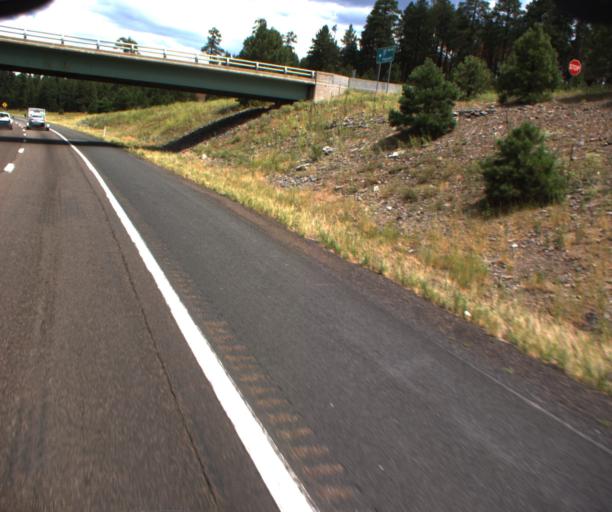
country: US
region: Arizona
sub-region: Coconino County
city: Mountainaire
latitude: 35.0516
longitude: -111.6826
